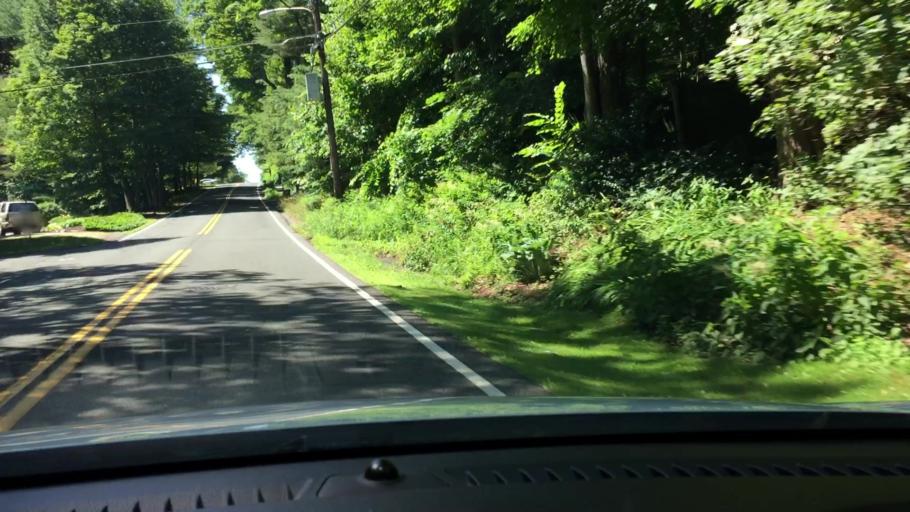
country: US
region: Massachusetts
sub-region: Berkshire County
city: Pittsfield
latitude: 42.4001
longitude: -73.2544
